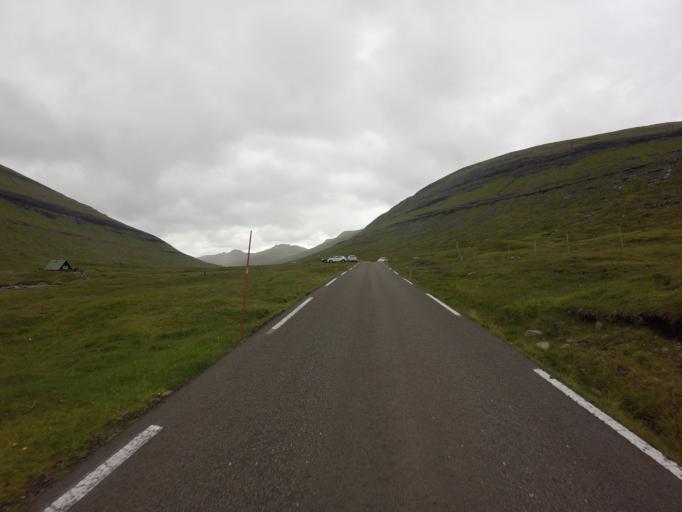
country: FO
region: Streymoy
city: Vestmanna
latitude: 62.2232
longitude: -7.1295
